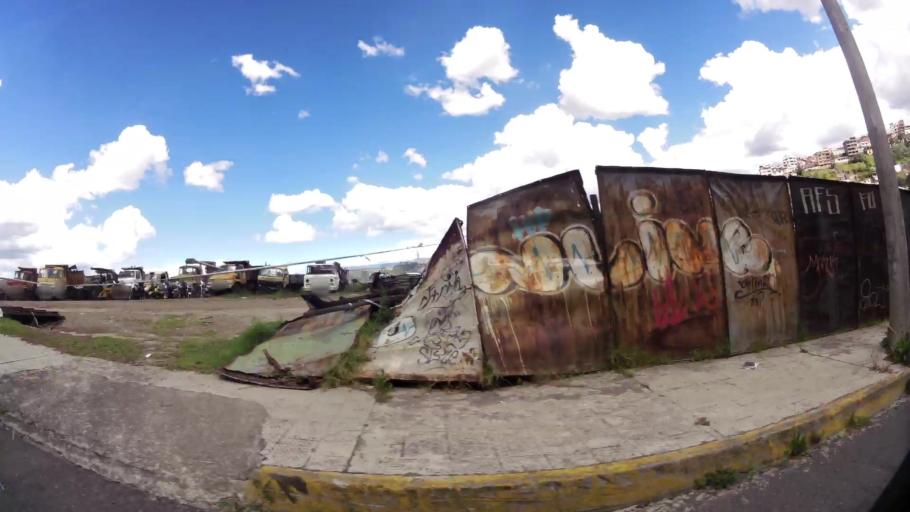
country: EC
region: Pichincha
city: Quito
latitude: -0.2053
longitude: -78.5110
